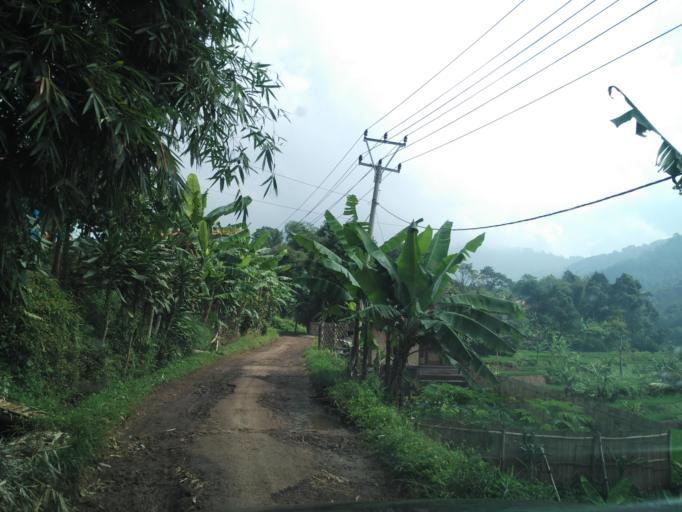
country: ID
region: West Java
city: Ciranjang-hilir
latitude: -6.7816
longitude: 107.1183
